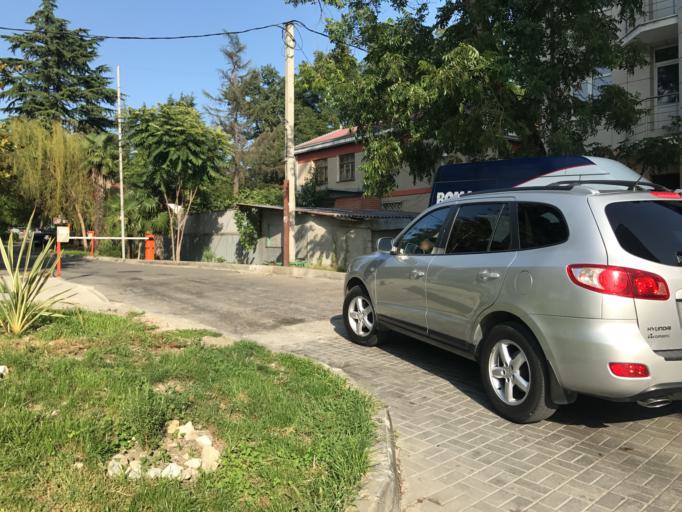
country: RU
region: Krasnodarskiy
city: Adler
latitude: 43.4205
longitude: 39.9380
